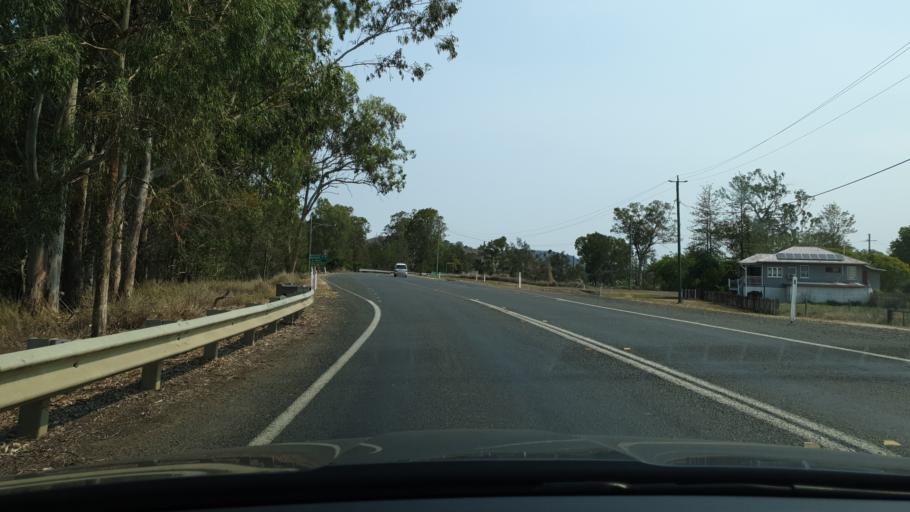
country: AU
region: Queensland
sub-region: Ipswich
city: Deebing Heights
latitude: -28.0060
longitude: 152.6805
